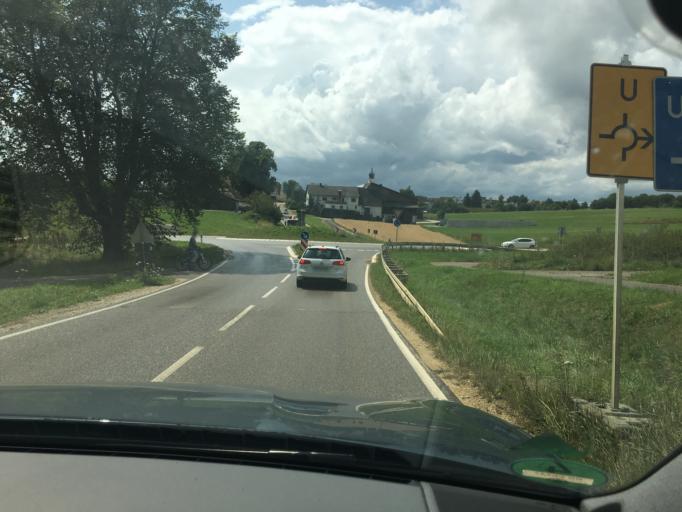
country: DE
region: Baden-Wuerttemberg
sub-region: Tuebingen Region
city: Merklingen
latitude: 48.5121
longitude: 9.7675
